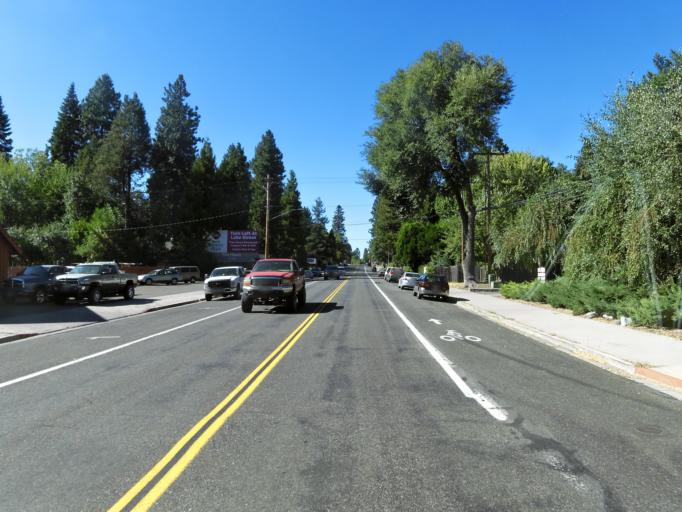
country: US
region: California
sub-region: Siskiyou County
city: Mount Shasta
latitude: 41.3028
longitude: -122.3073
